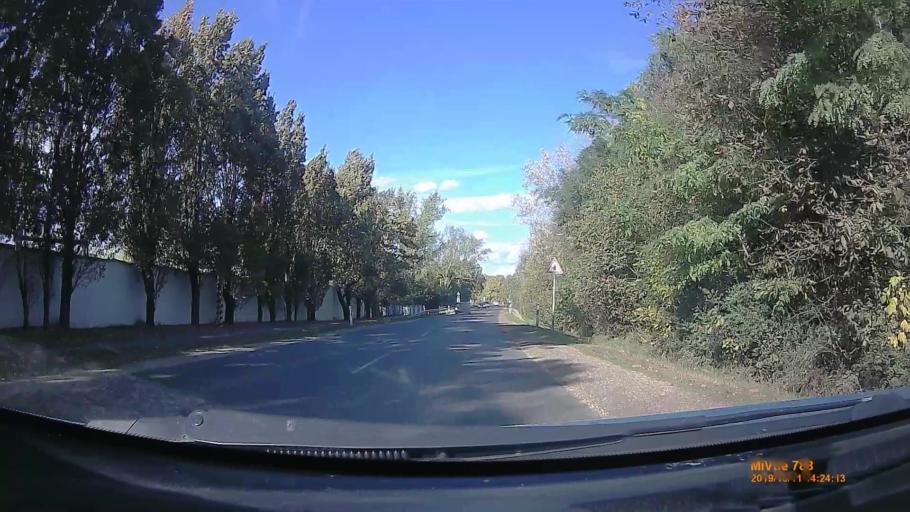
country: HU
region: Hajdu-Bihar
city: Balmazujvaros
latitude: 47.5323
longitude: 21.3565
